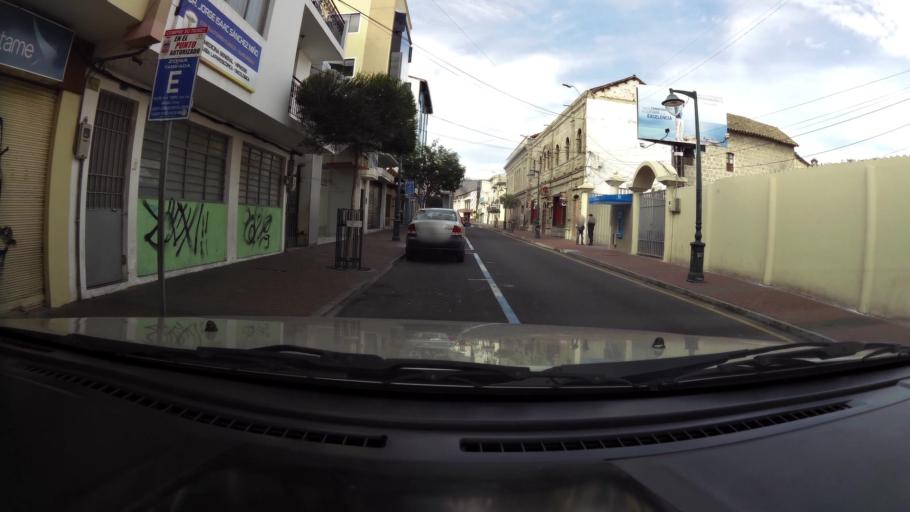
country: EC
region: Tungurahua
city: Ambato
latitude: -1.2447
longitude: -78.6298
